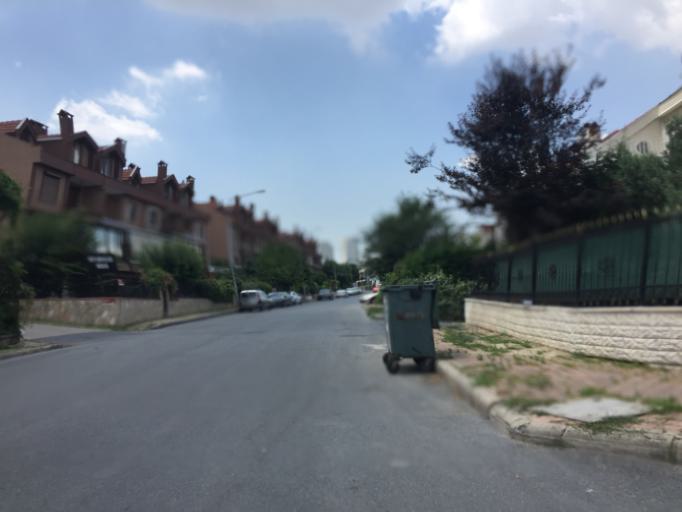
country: TR
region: Istanbul
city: Esenyurt
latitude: 41.0808
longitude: 28.6690
